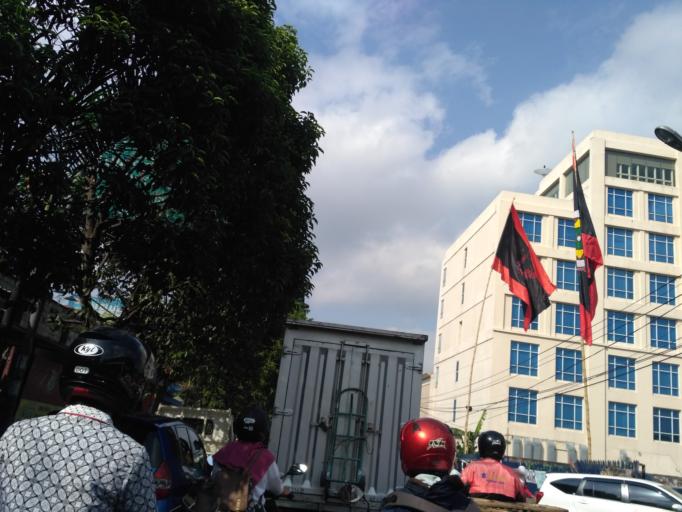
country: ID
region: Daerah Istimewa Yogyakarta
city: Yogyakarta
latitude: -7.8001
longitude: 110.3563
